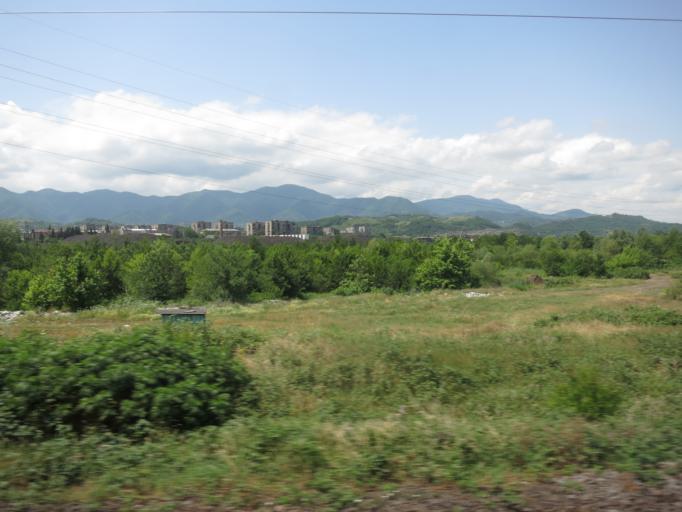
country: GE
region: Imereti
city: Zestap'oni
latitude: 42.1158
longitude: 43.0195
